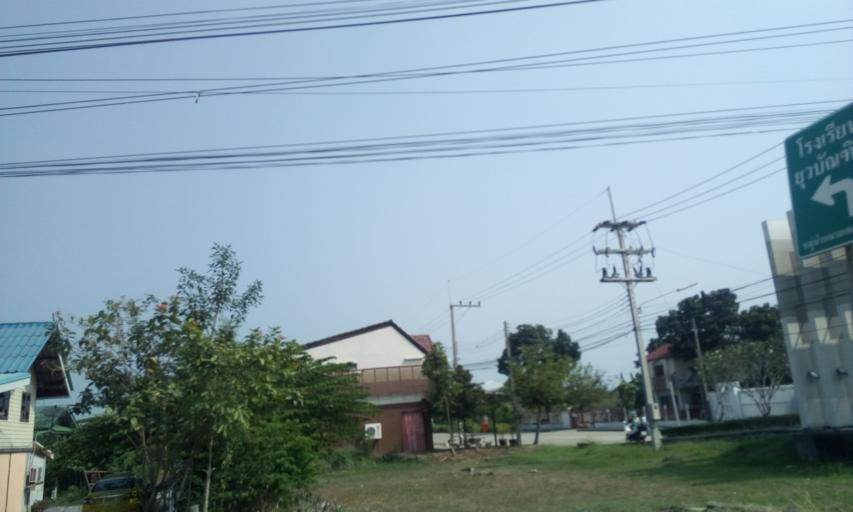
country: TH
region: Pathum Thani
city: Ban Lam Luk Ka
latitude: 13.9779
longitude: 100.7532
